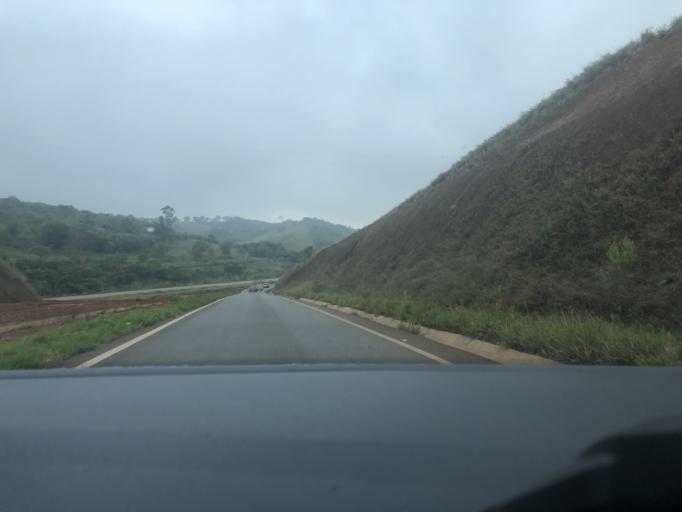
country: BR
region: Minas Gerais
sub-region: Congonhas
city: Congonhas
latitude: -20.6019
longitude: -43.9345
